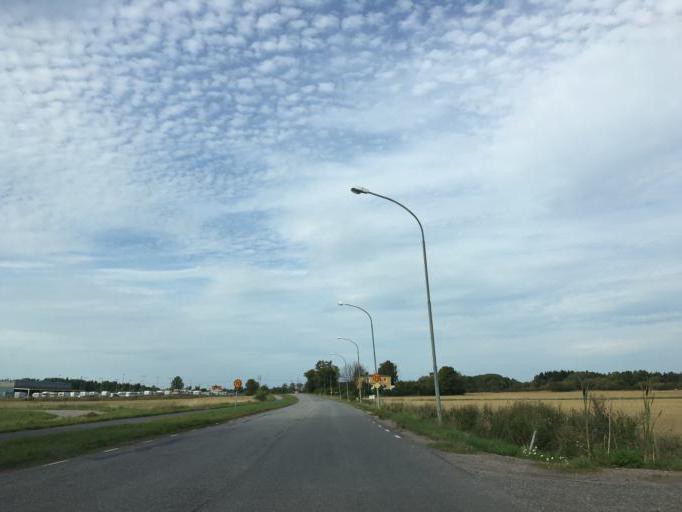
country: SE
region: Soedermanland
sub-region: Eskilstuna Kommun
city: Torshalla
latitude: 59.4290
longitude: 16.4735
